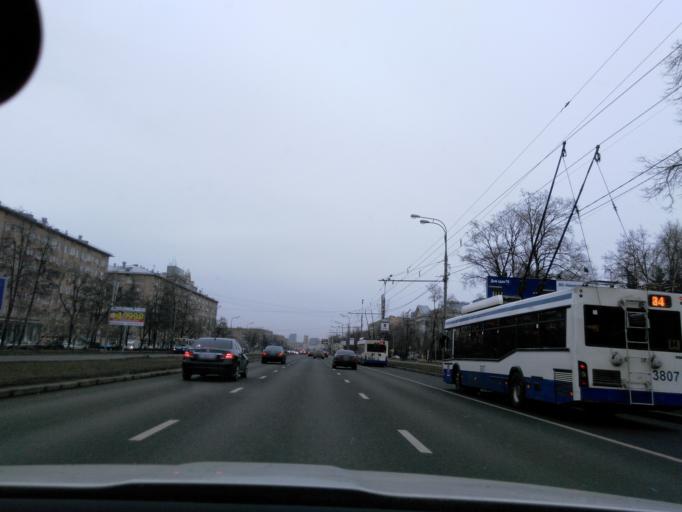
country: RU
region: Moskovskaya
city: Leninskiye Gory
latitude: 55.7007
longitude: 37.5678
